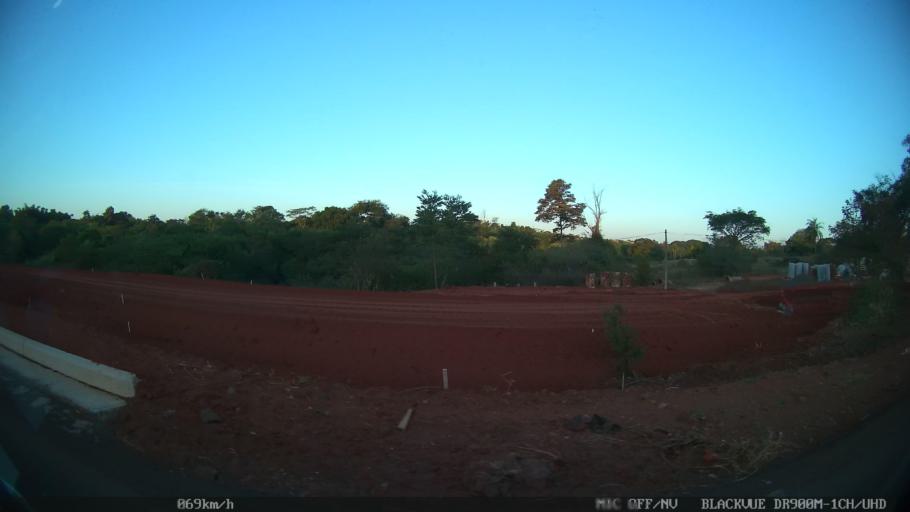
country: BR
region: Sao Paulo
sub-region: Sao Jose Do Rio Preto
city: Sao Jose do Rio Preto
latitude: -20.7774
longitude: -49.3524
